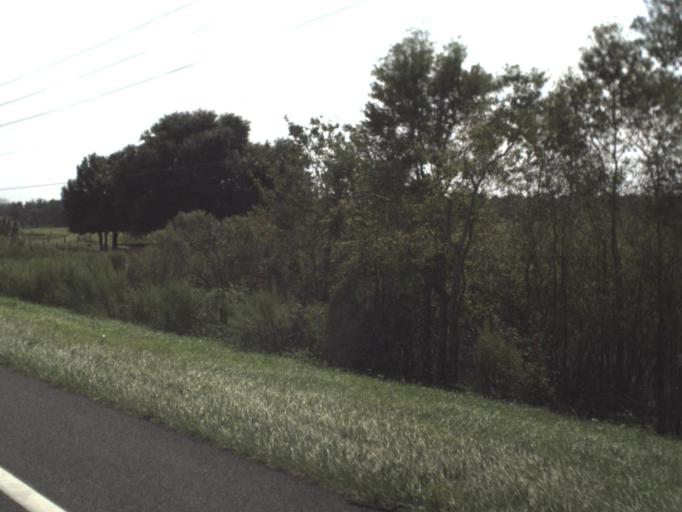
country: US
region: Florida
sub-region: Polk County
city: Dundee
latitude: 28.0053
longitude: -81.6315
